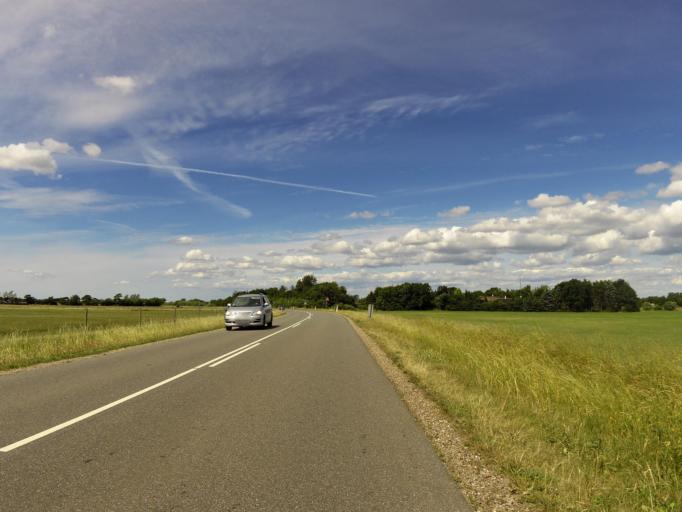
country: DK
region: South Denmark
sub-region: Esbjerg Kommune
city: Ribe
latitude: 55.3124
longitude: 8.7618
